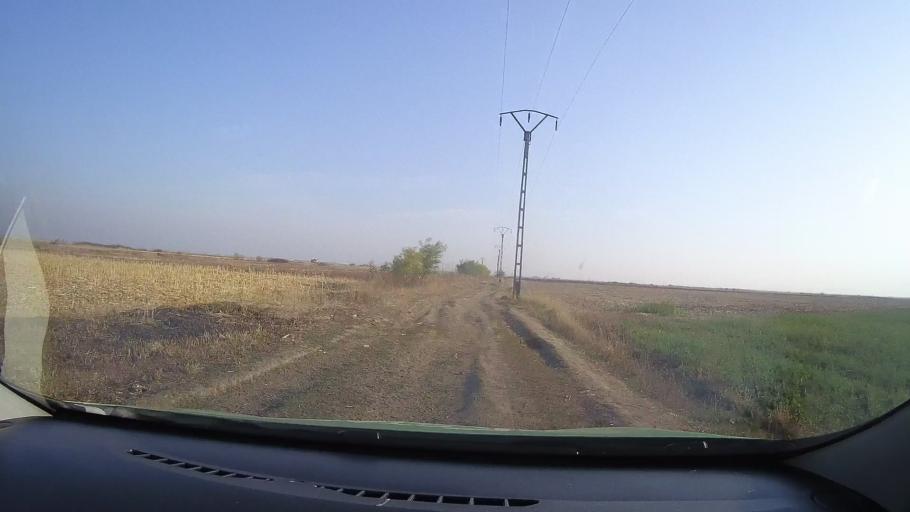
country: RO
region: Arad
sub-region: Comuna Graniceri
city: Graniceri
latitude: 46.5382
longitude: 21.3247
